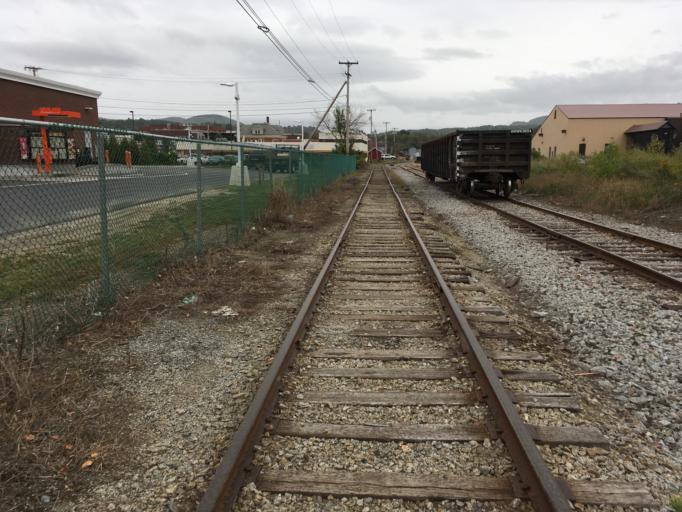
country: US
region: Vermont
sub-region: Washington County
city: Barre
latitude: 44.2016
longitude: -72.5081
